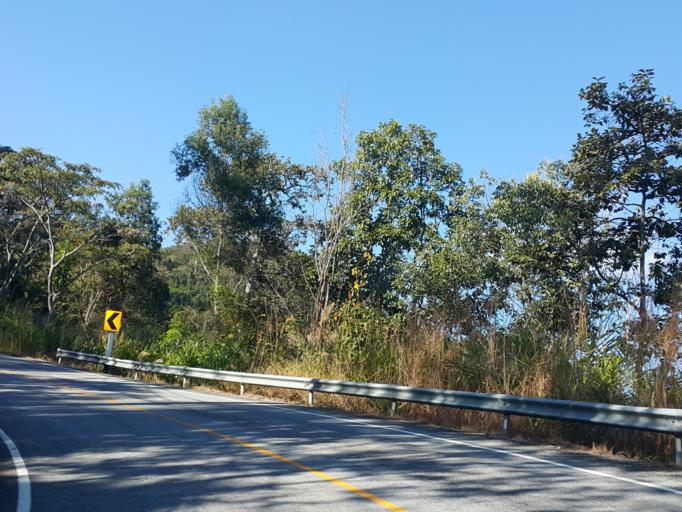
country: TH
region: Chiang Mai
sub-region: Amphoe Chiang Dao
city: Chiang Dao
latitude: 19.5284
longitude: 98.8826
